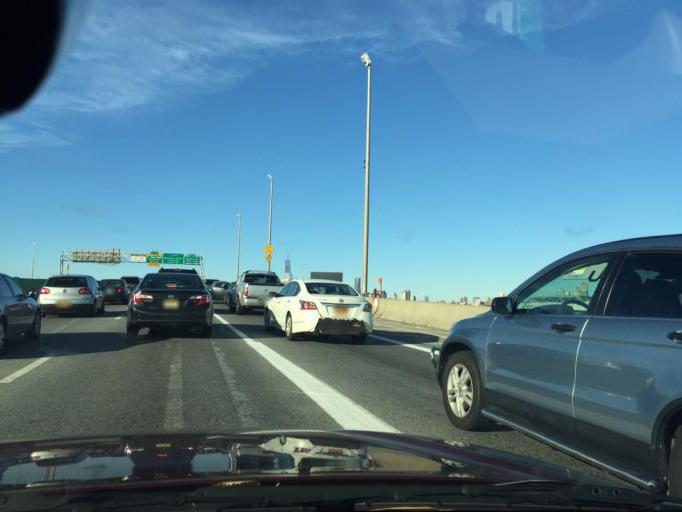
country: US
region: New York
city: New York City
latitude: 40.6702
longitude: -73.9974
